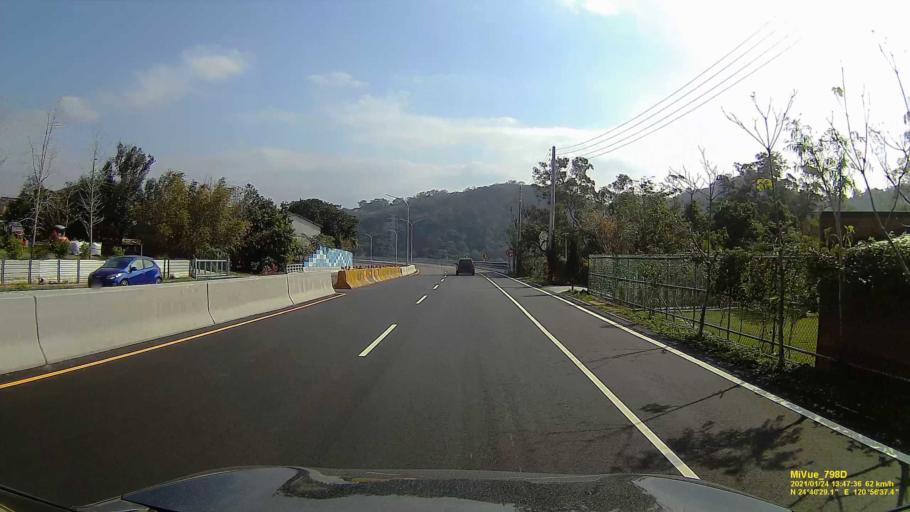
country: TW
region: Taiwan
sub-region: Hsinchu
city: Hsinchu
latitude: 24.6746
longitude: 120.9438
